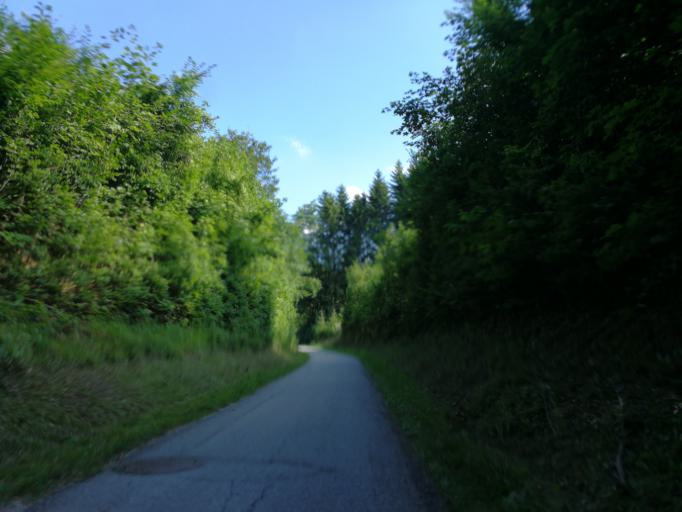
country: AT
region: Salzburg
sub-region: Politischer Bezirk Salzburg-Umgebung
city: Hallwang
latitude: 47.8454
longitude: 13.0885
